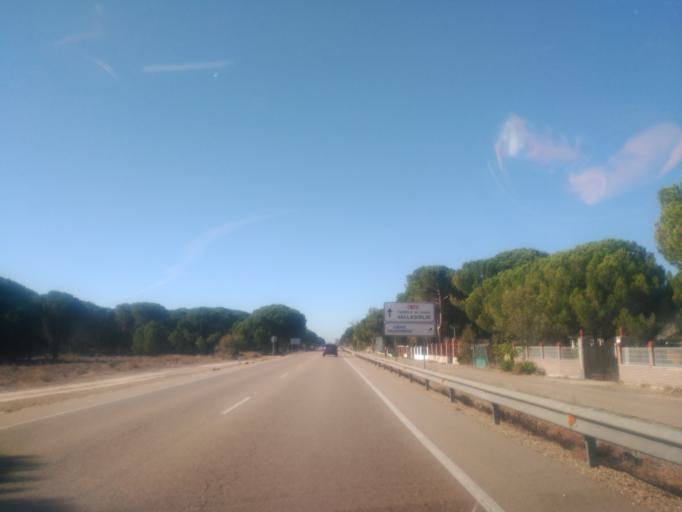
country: ES
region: Castille and Leon
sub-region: Provincia de Valladolid
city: Villabanez
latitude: 41.5962
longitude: -4.5123
